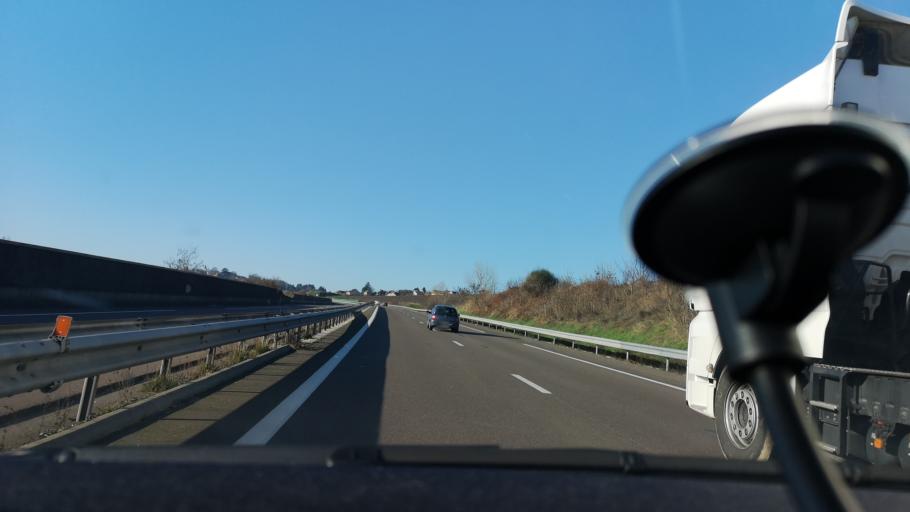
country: FR
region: Bourgogne
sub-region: Departement de Saone-et-Loire
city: Buxy
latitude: 46.7568
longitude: 4.7022
